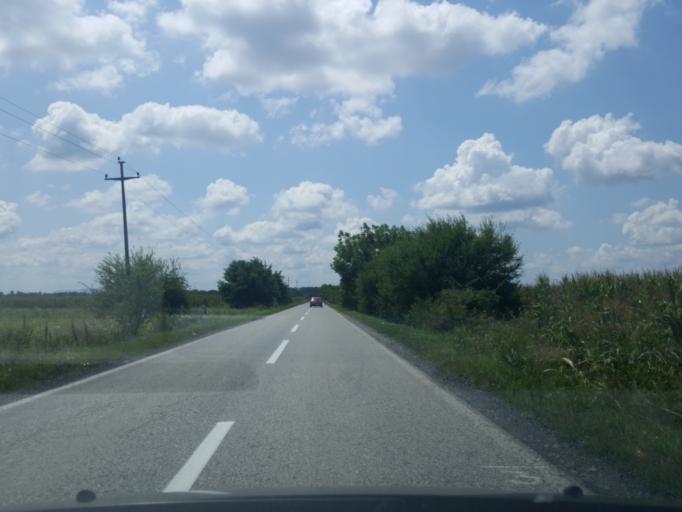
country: RS
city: Metkovic
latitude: 44.8694
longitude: 19.5478
